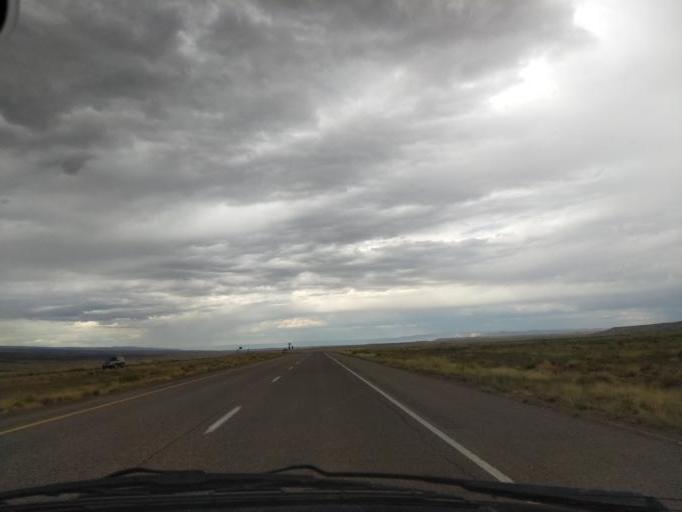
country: US
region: Colorado
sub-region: Delta County
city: Delta
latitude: 38.8486
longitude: -108.3043
